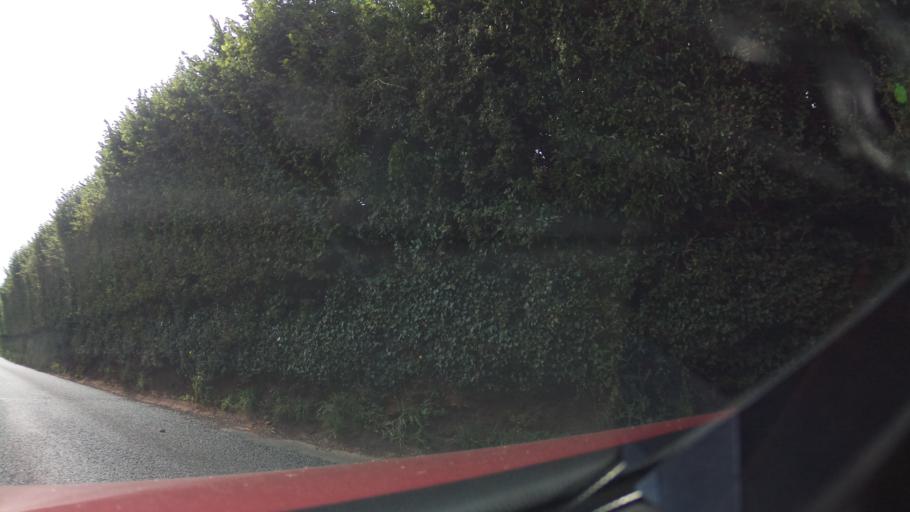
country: GB
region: England
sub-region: North Somerset
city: Winford
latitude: 51.3802
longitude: -2.6586
